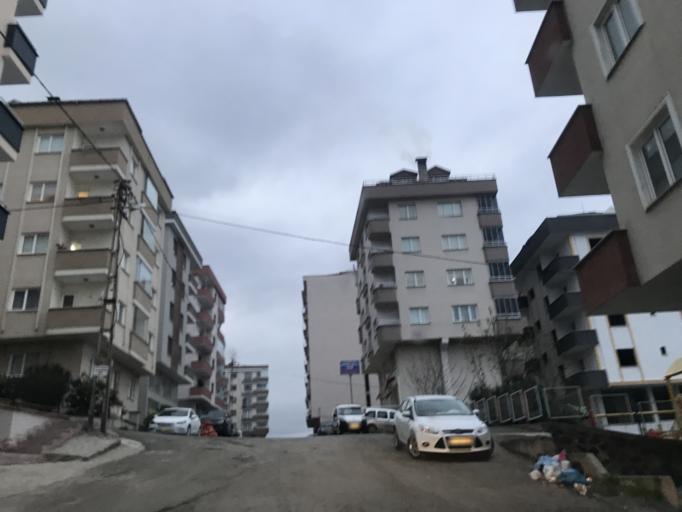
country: TR
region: Trabzon
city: Akcaabat
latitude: 41.0158
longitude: 39.5886
